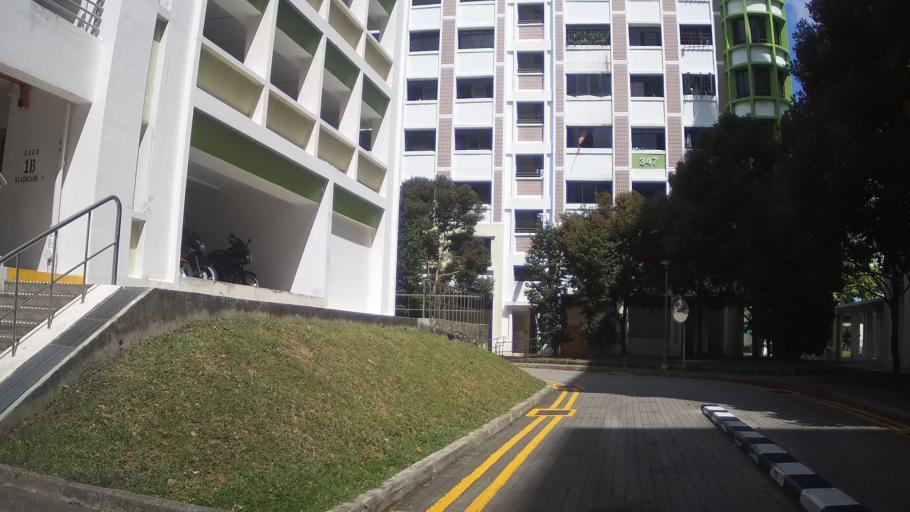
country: MY
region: Johor
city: Johor Bahru
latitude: 1.3402
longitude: 103.7207
